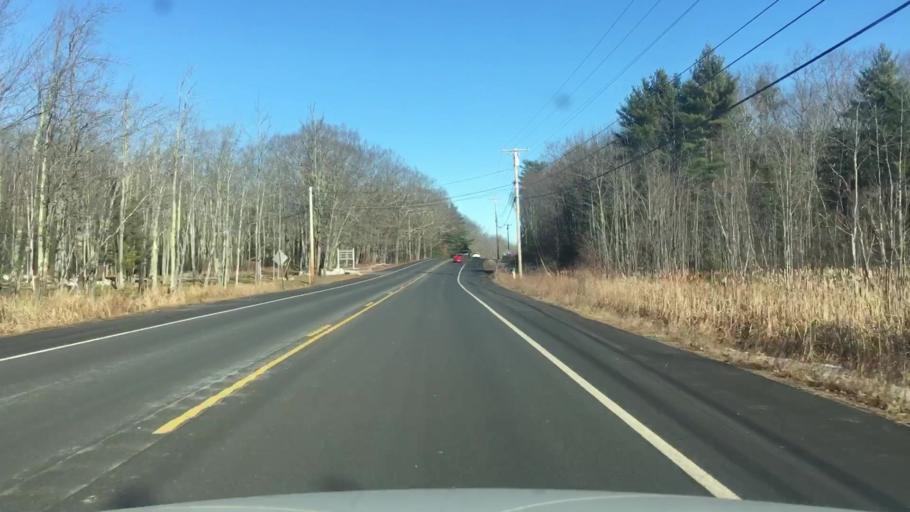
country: US
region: Maine
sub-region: York County
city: Arundel
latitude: 43.4435
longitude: -70.5016
